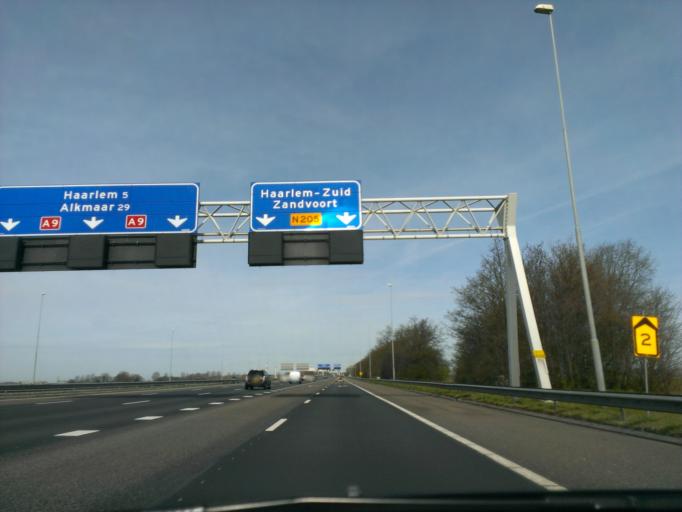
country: NL
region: North Holland
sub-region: Gemeente Haarlemmermeer
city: Hoofddorp
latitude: 52.3665
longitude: 4.7223
